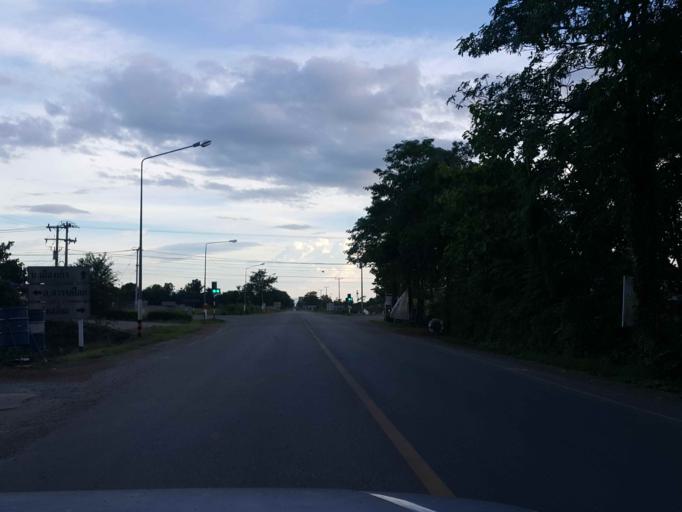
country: TH
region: Sukhothai
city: Sawankhalok
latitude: 17.3099
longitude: 99.7330
